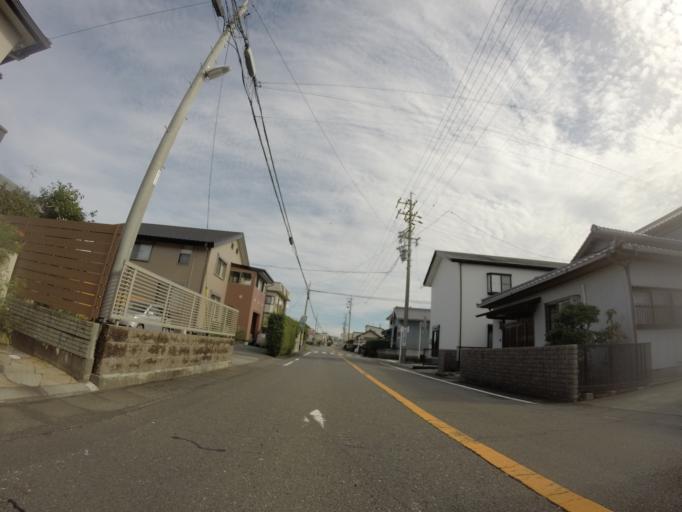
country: JP
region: Shizuoka
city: Sagara
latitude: 34.7554
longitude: 138.2504
